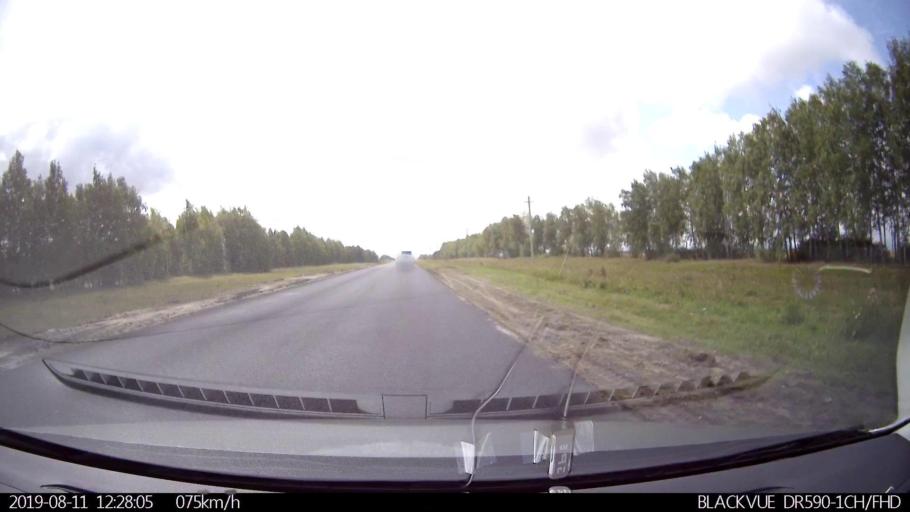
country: RU
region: Ulyanovsk
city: Ignatovka
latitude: 53.8474
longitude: 47.9146
